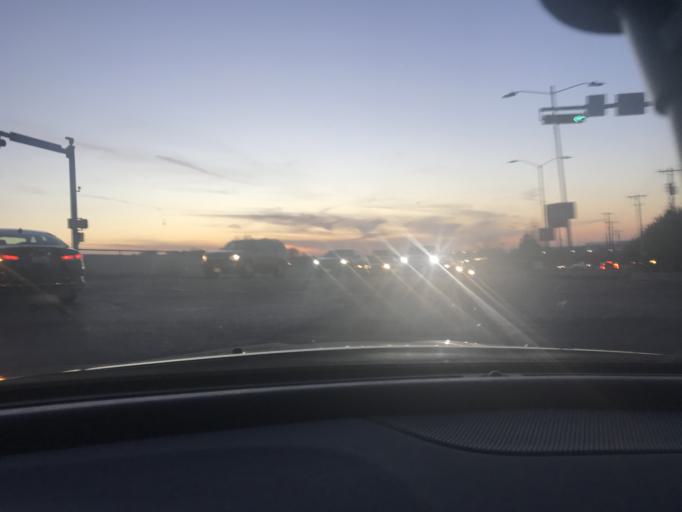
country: US
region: Texas
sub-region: Tarrant County
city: Arlington
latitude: 32.7603
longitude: -97.1144
